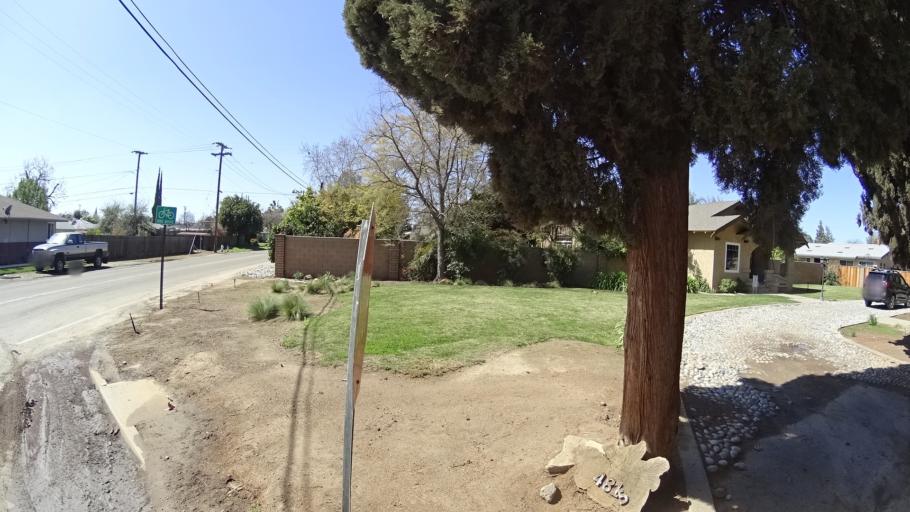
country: US
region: California
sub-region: Fresno County
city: Fresno
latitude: 36.8048
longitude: -119.8152
